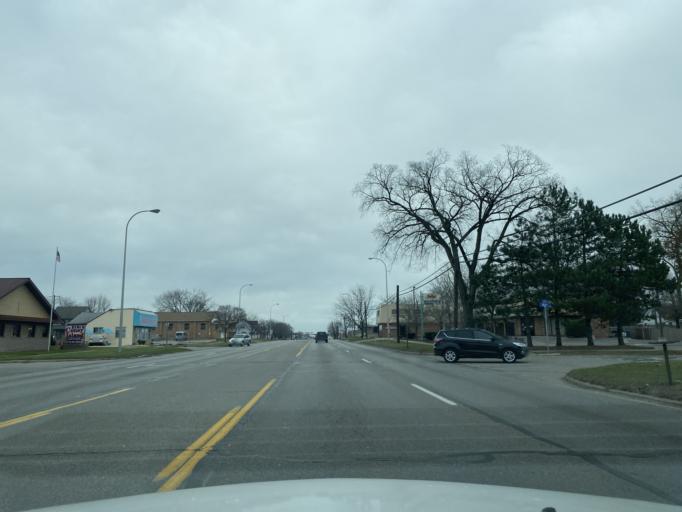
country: US
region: Michigan
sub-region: Wayne County
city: Taylor
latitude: 42.1974
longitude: -83.2729
